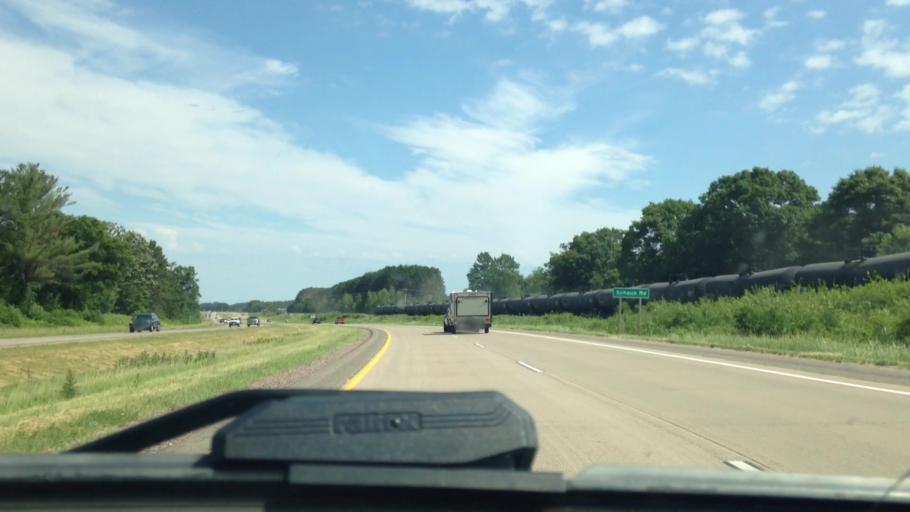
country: US
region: Wisconsin
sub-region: Washburn County
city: Spooner
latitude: 45.8686
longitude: -91.8310
